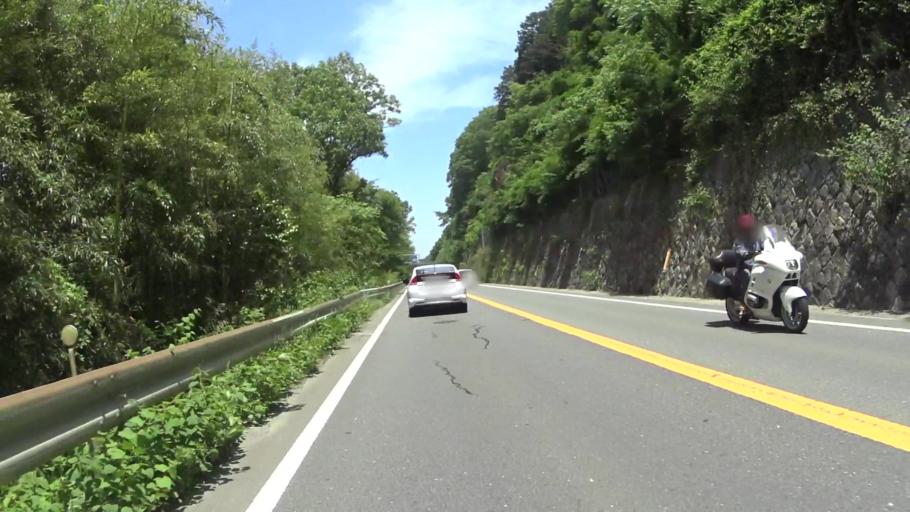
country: JP
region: Kyoto
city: Kameoka
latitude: 35.1446
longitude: 135.4271
